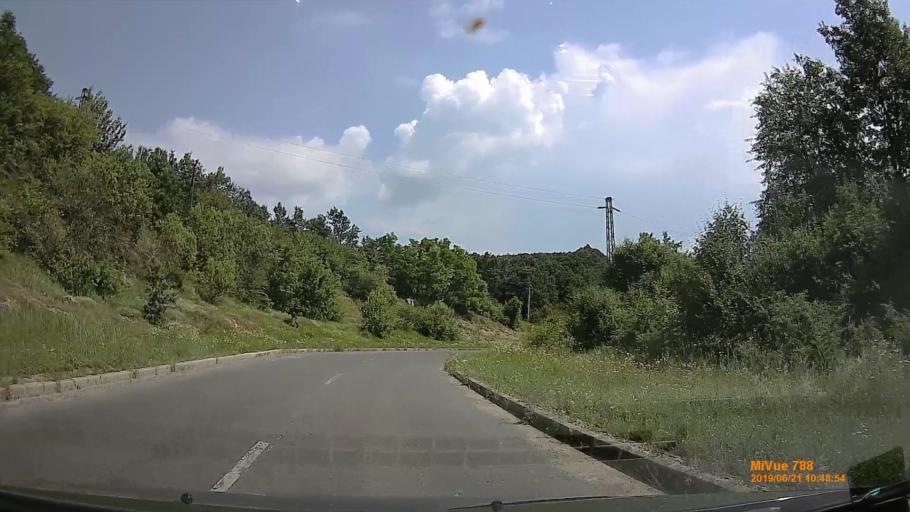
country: HU
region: Baranya
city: Buekkoesd
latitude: 46.1263
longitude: 18.0300
